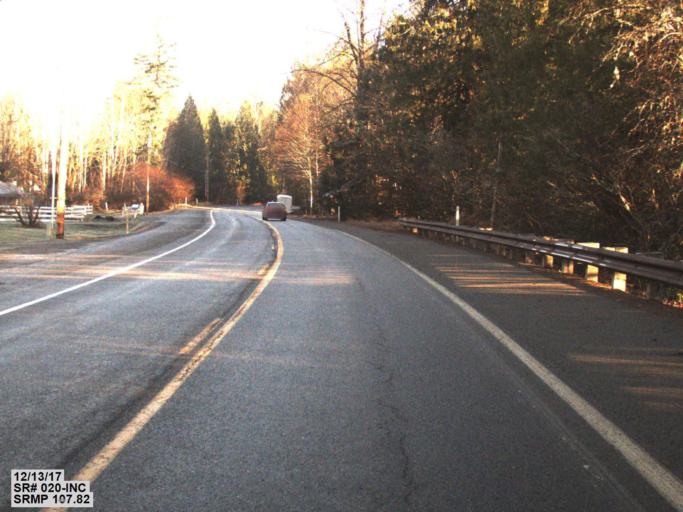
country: US
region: Washington
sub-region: Snohomish County
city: Darrington
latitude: 48.5507
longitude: -121.4229
